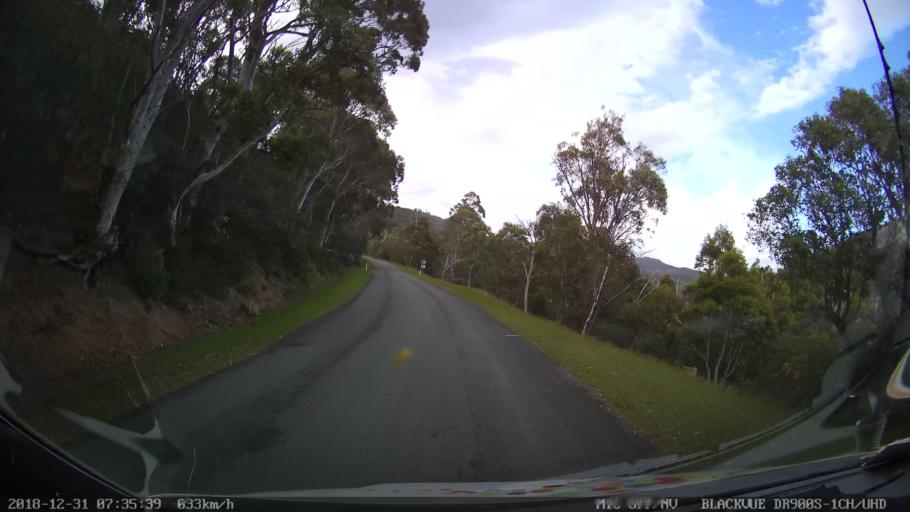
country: AU
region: New South Wales
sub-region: Snowy River
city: Jindabyne
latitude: -36.3359
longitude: 148.4442
